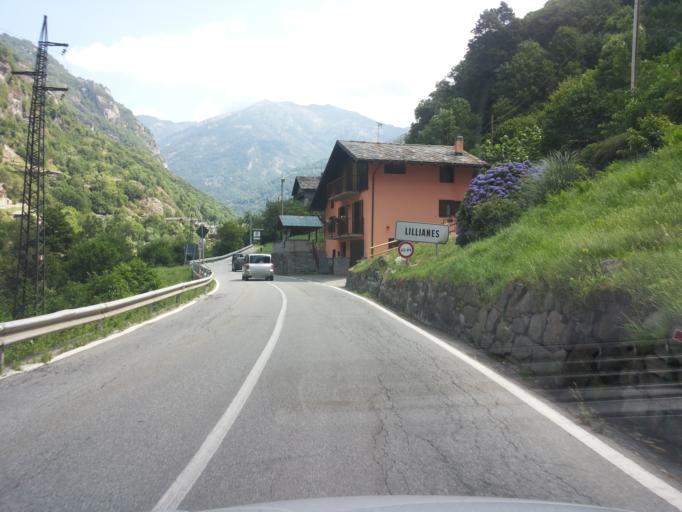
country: IT
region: Aosta Valley
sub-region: Valle d'Aosta
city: Lillianes
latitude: 45.6265
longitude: 7.8343
